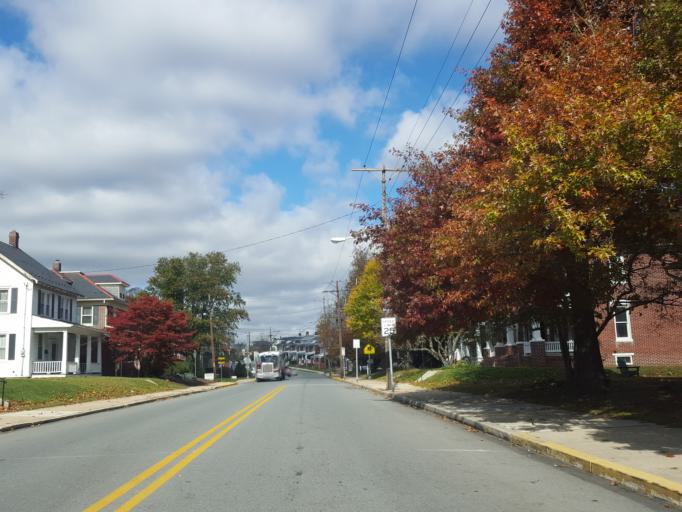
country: US
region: Pennsylvania
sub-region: York County
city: Red Lion
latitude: 39.8960
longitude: -76.6002
